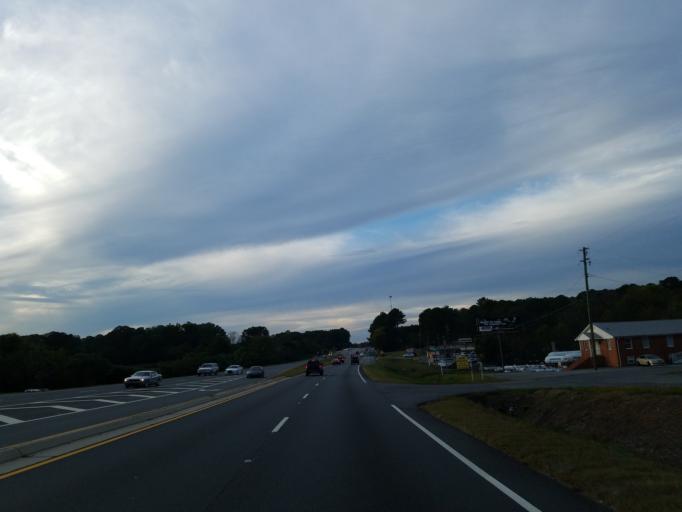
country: US
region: Georgia
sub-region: Bartow County
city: Cartersville
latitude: 34.2112
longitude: -84.8301
